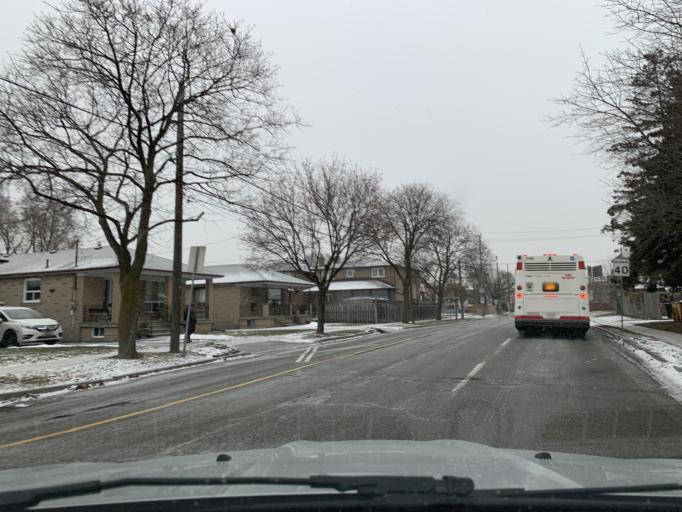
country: CA
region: Ontario
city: Toronto
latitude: 43.7320
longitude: -79.4689
